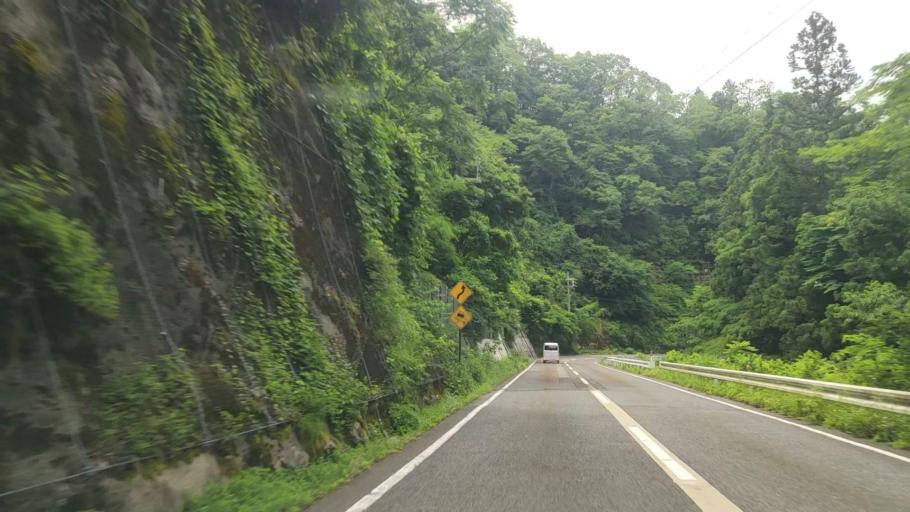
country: JP
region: Hyogo
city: Toyooka
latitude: 35.4773
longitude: 134.6053
